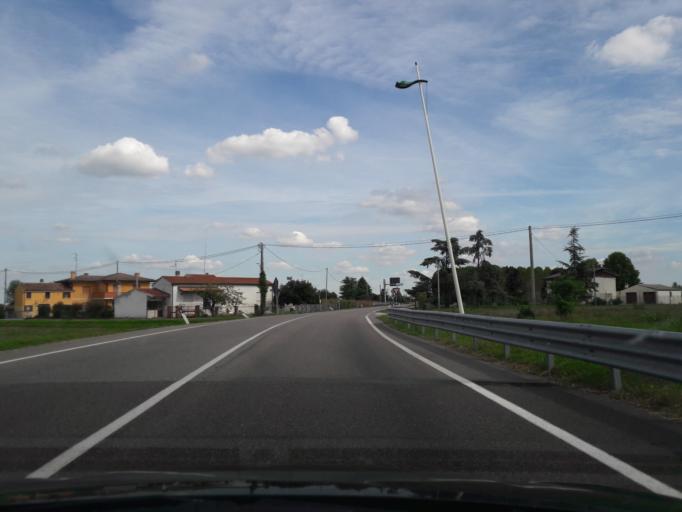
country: IT
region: Veneto
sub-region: Provincia di Rovigo
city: Badia Polesine
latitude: 45.0918
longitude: 11.5286
